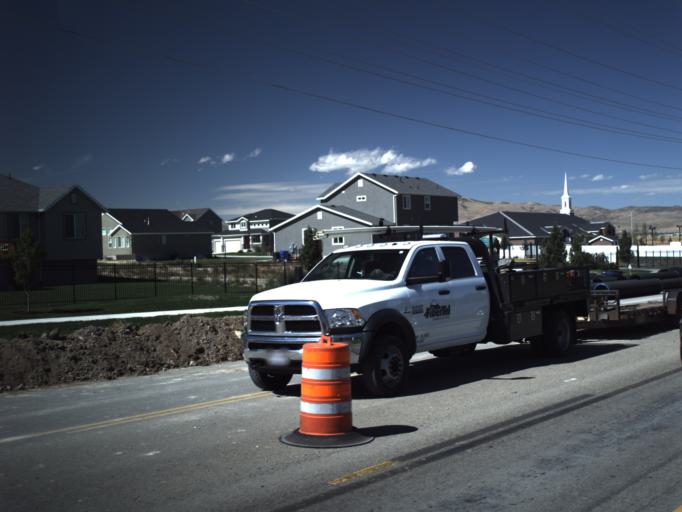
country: US
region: Utah
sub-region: Utah County
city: Saratoga Springs
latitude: 40.3389
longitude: -111.9159
